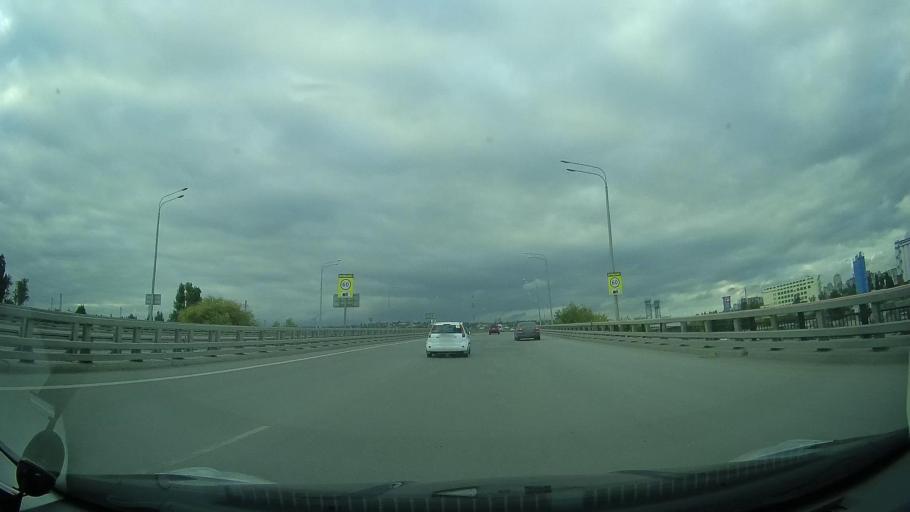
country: RU
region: Rostov
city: Rostov-na-Donu
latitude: 47.2033
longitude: 39.7111
